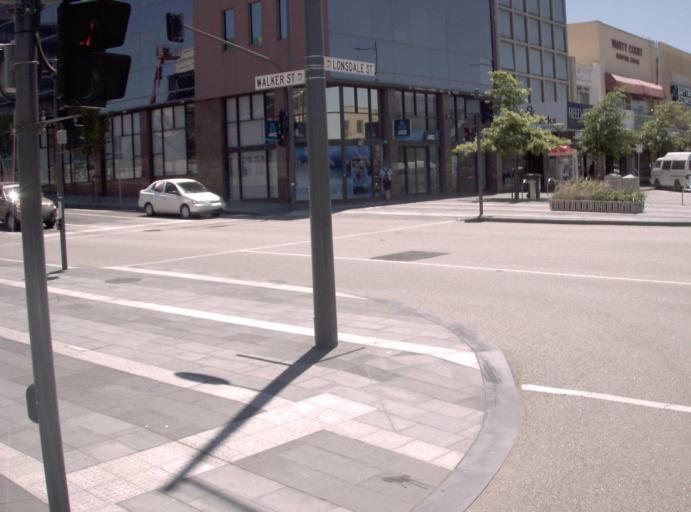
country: AU
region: Victoria
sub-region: Greater Dandenong
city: Dandenong
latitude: -37.9882
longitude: 145.2143
